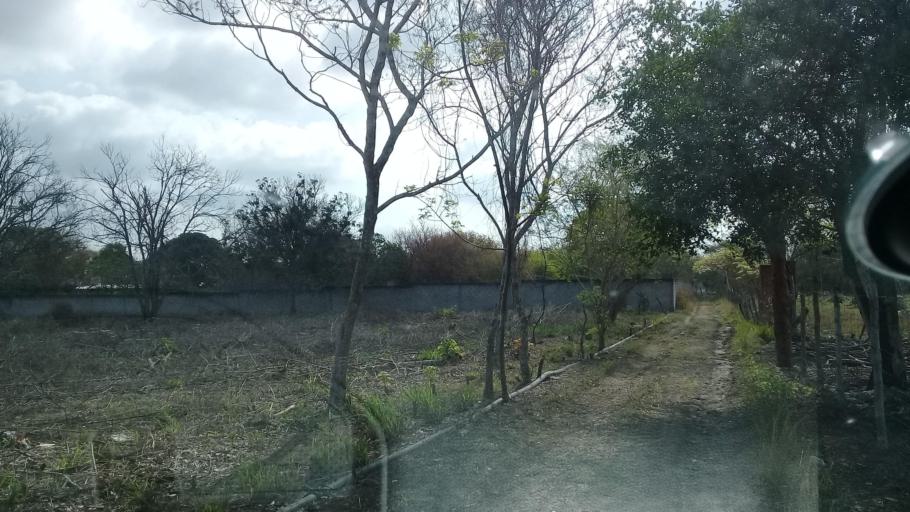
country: MX
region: Veracruz
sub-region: Emiliano Zapata
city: Plan del Rio
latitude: 19.3867
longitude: -96.6413
